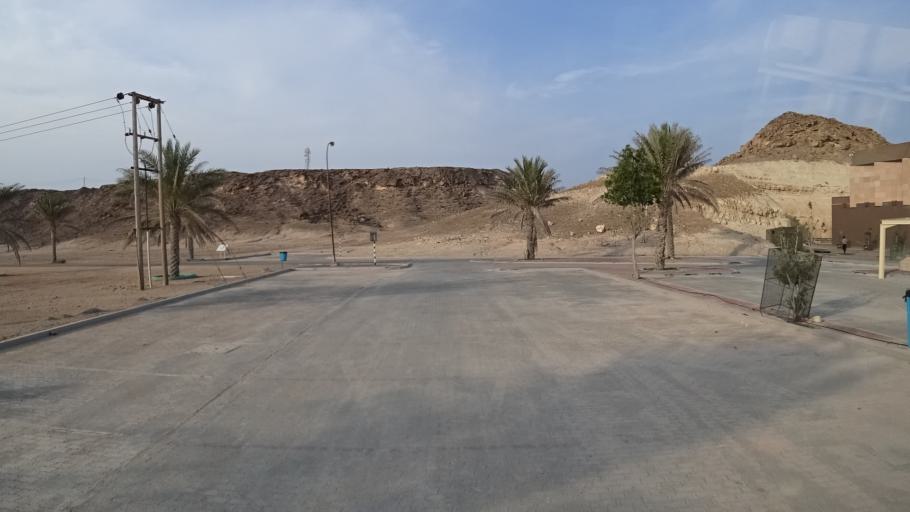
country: OM
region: Ash Sharqiyah
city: Sur
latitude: 22.4260
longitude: 59.8268
